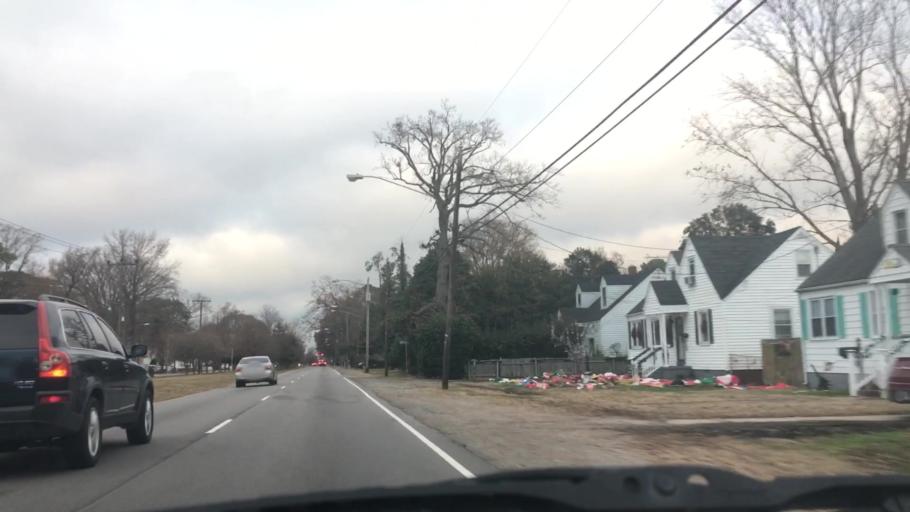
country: US
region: Virginia
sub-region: City of Norfolk
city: Norfolk
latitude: 36.9198
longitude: -76.2421
